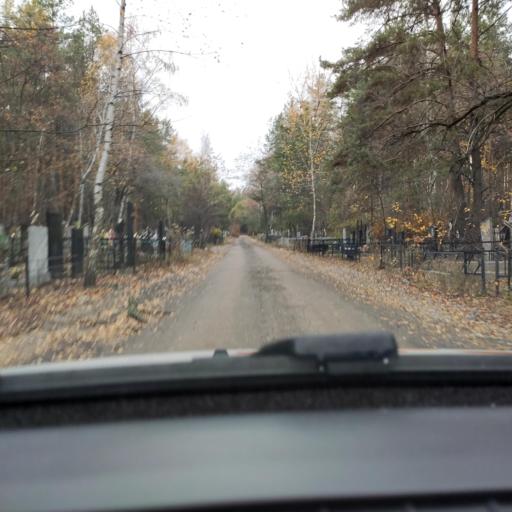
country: RU
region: Voronezj
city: Pridonskoy
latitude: 51.6723
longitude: 39.1137
